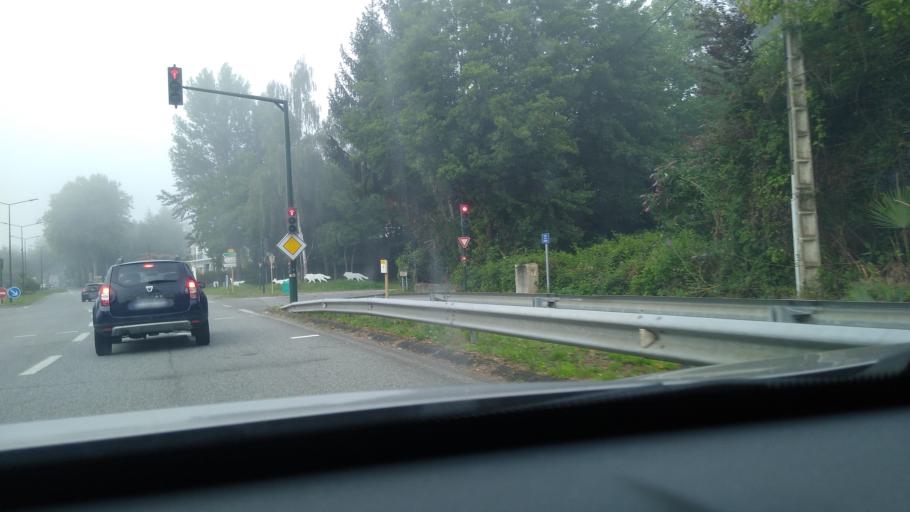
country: FR
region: Midi-Pyrenees
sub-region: Departement de la Haute-Garonne
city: Salies-du-Salat
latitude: 43.0914
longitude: 0.9500
